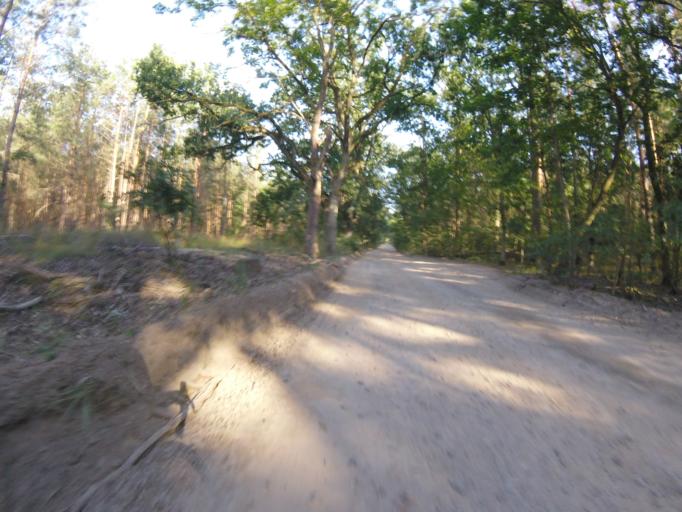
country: DE
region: Brandenburg
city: Zossen
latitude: 52.2043
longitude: 13.4941
